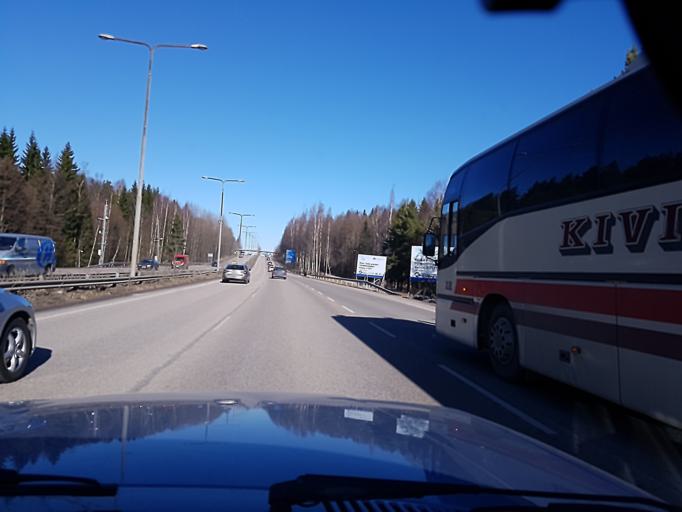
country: FI
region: Uusimaa
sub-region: Helsinki
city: Helsinki
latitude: 60.2285
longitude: 24.9063
